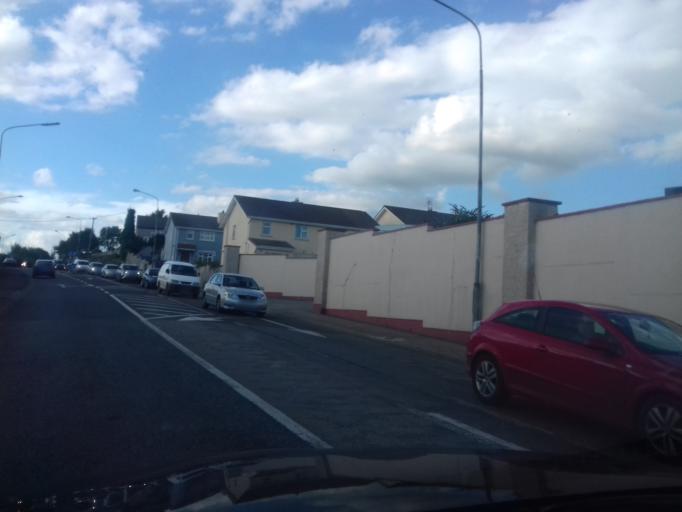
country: IE
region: Leinster
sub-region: Loch Garman
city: New Ross
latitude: 52.3988
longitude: -6.9361
